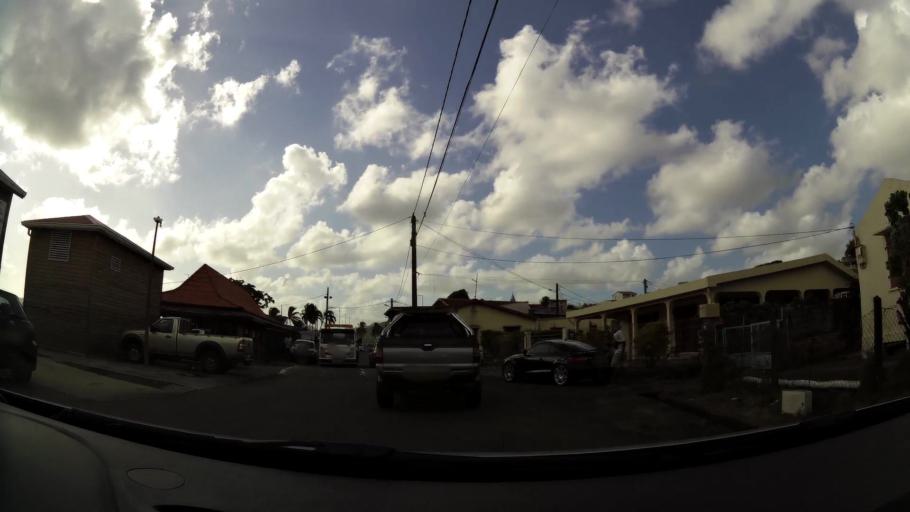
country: MQ
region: Martinique
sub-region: Martinique
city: Le Robert
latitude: 14.6801
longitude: -60.9381
